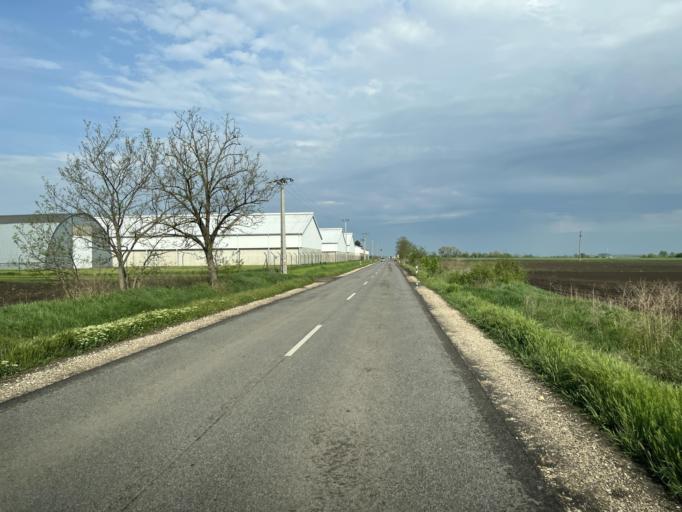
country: HU
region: Pest
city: Tapioszentmarton
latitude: 47.3156
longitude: 19.7556
